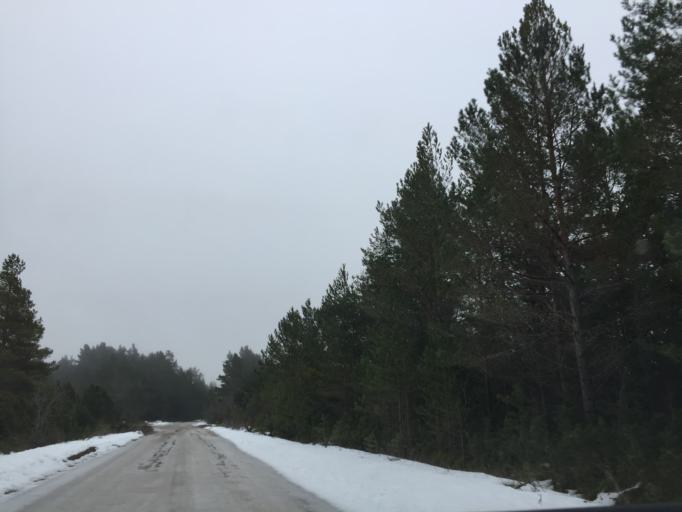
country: EE
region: Saare
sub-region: Kuressaare linn
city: Kuressaare
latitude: 58.4991
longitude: 21.9804
